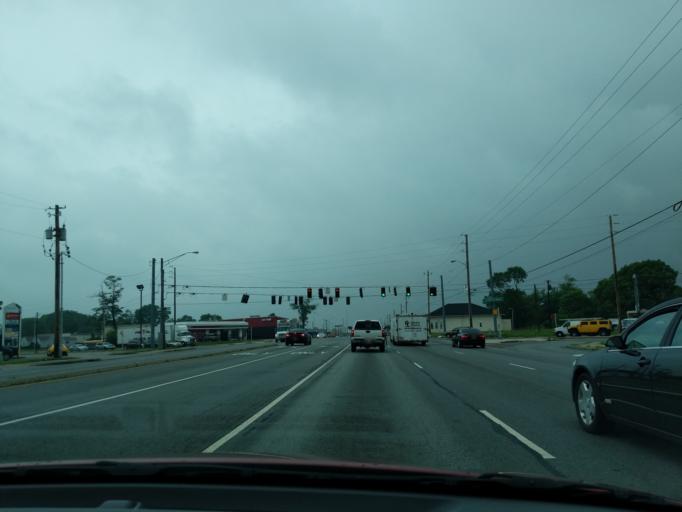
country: US
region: Indiana
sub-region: Marion County
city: Lawrence
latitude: 39.8368
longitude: -86.0263
